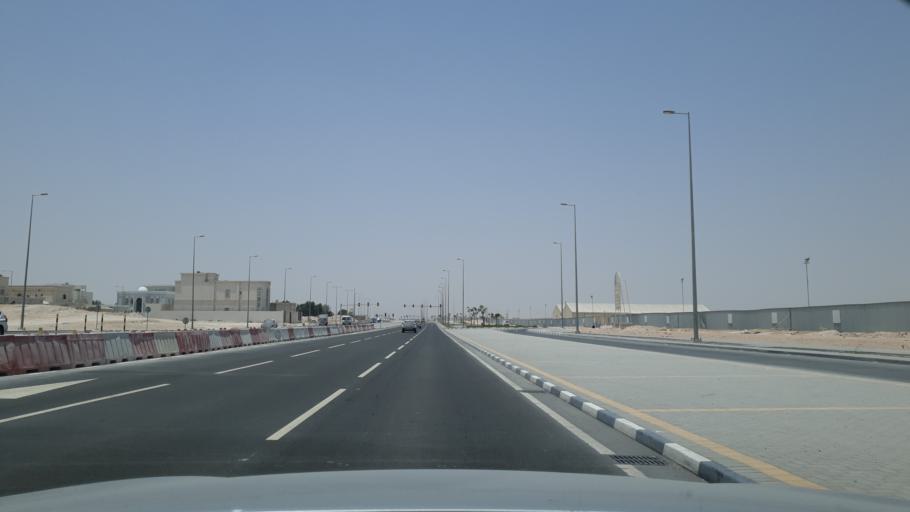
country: QA
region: Baladiyat Umm Salal
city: Umm Salal Muhammad
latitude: 25.4176
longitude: 51.4469
